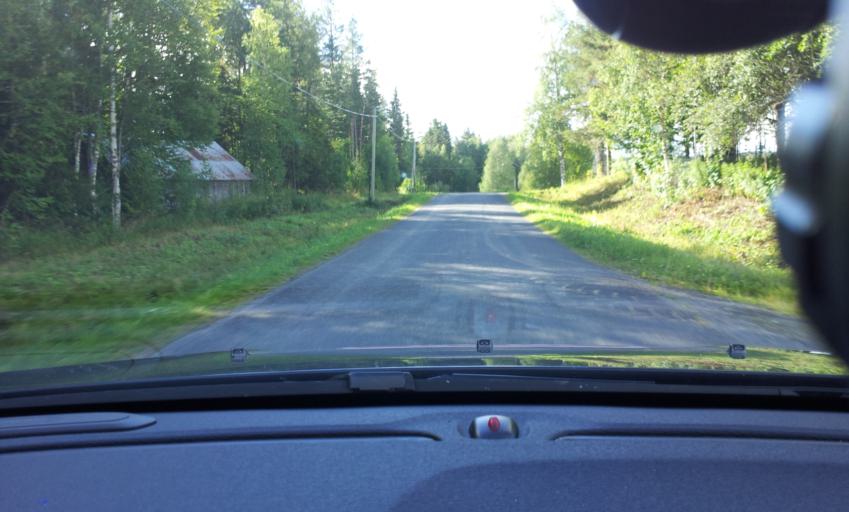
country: SE
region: Jaemtland
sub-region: Krokoms Kommun
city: Valla
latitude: 63.2665
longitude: 13.8526
